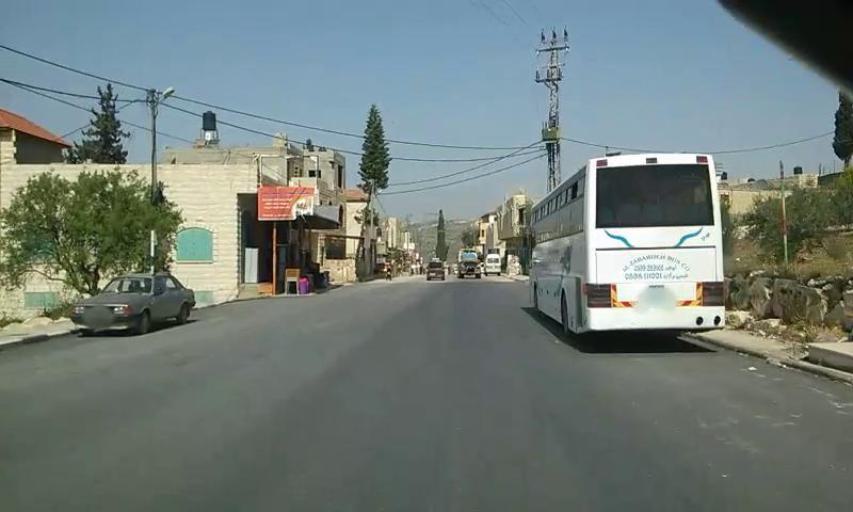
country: PS
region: West Bank
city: Az Zababidah
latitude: 32.3869
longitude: 35.3227
